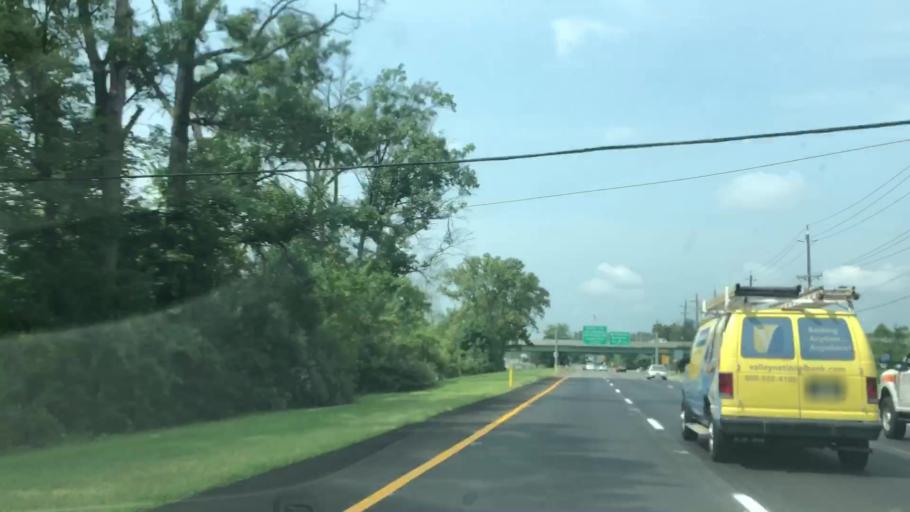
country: US
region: New Jersey
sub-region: Passaic County
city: Singac
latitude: 40.8932
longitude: -74.2603
